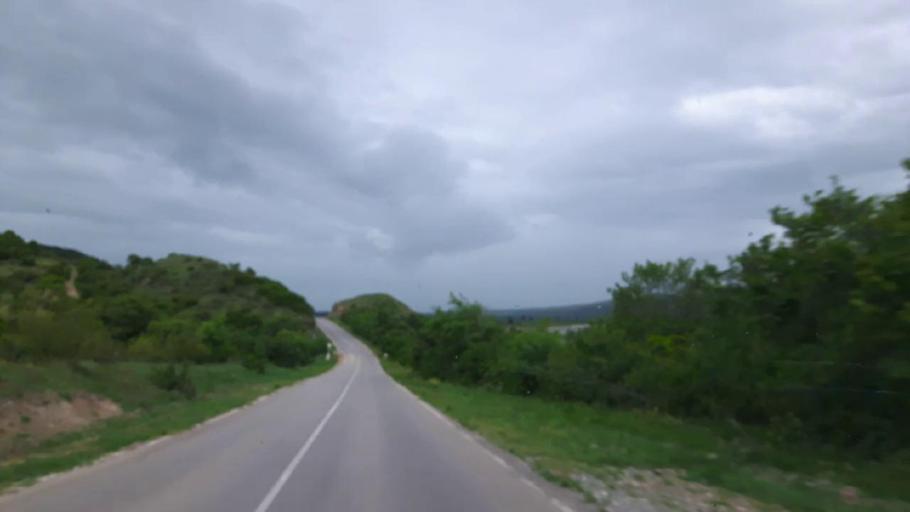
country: GE
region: Shida Kartli
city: Gori
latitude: 41.9889
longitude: 44.0419
